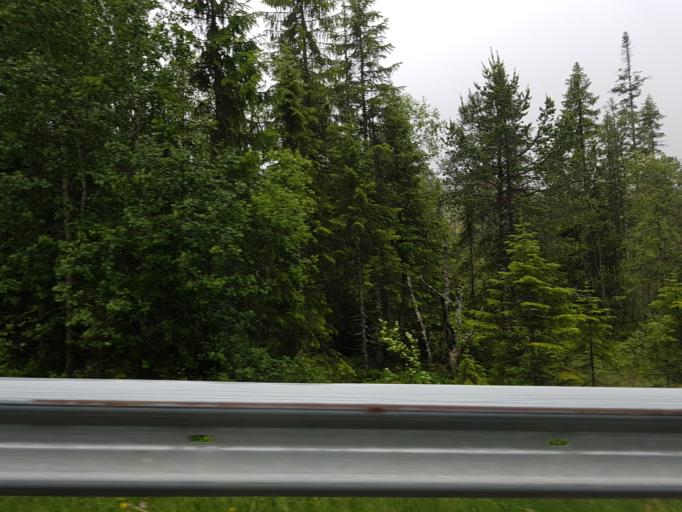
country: NO
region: Sor-Trondelag
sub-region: Selbu
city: Mebonden
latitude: 63.3380
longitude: 11.0877
